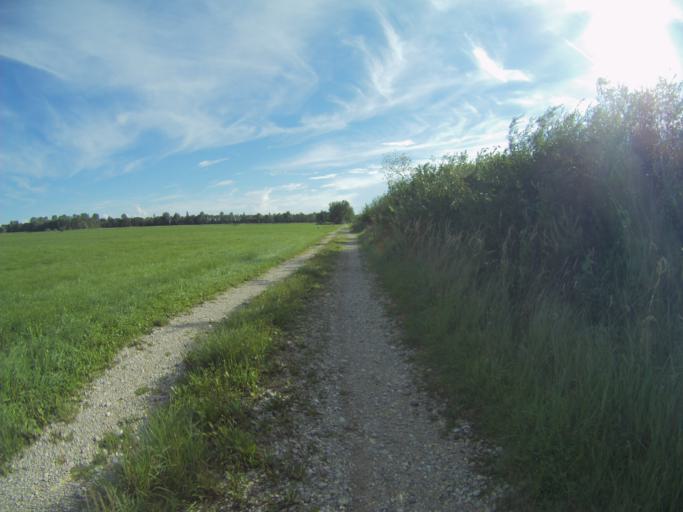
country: DE
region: Bavaria
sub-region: Upper Bavaria
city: Marzling
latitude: 48.3798
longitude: 11.7948
